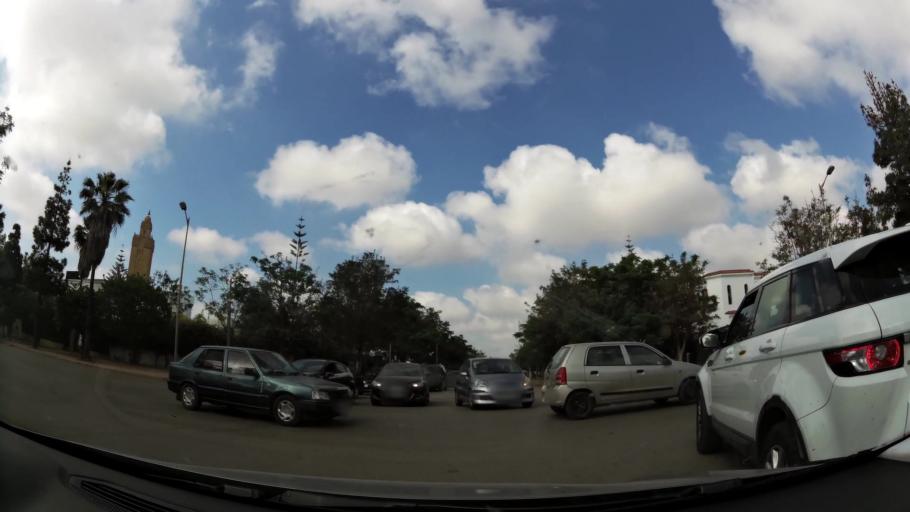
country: MA
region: Rabat-Sale-Zemmour-Zaer
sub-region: Skhirate-Temara
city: Temara
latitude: 33.9518
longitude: -6.8707
